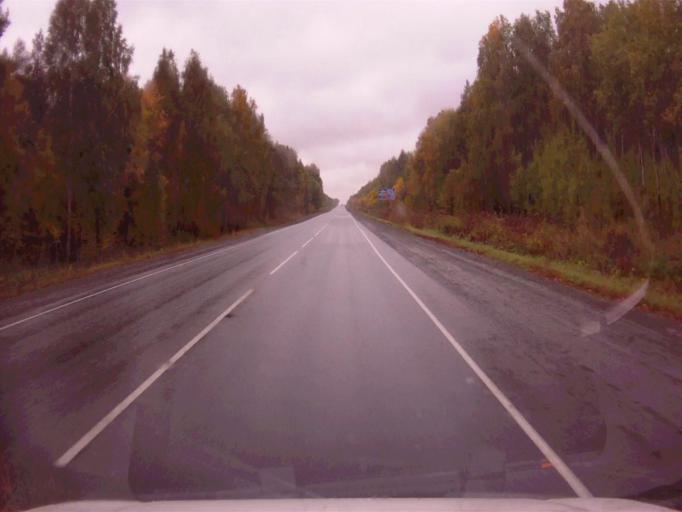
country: RU
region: Chelyabinsk
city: Roshchino
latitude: 55.3726
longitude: 61.1561
